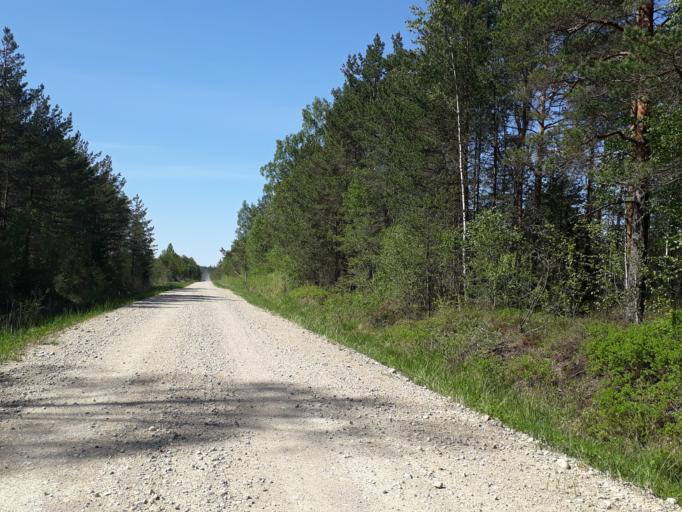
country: EE
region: Paernumaa
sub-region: Vaendra vald (alev)
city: Vandra
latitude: 58.7392
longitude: 24.9915
